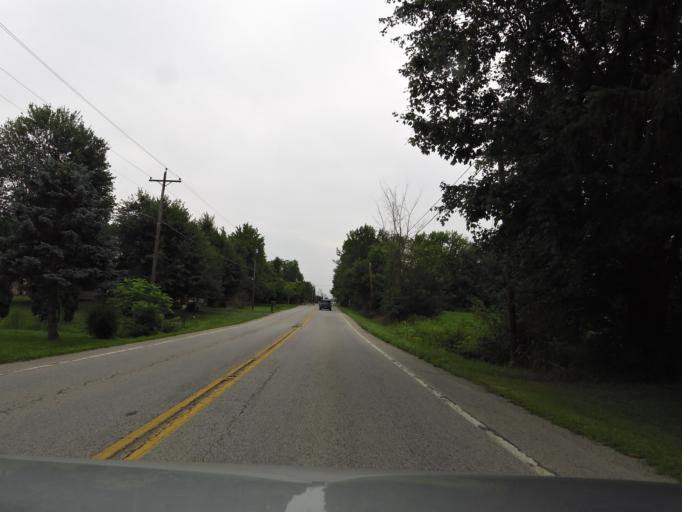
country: US
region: Ohio
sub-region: Brown County
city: Mount Orab
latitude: 39.0515
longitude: -83.9236
